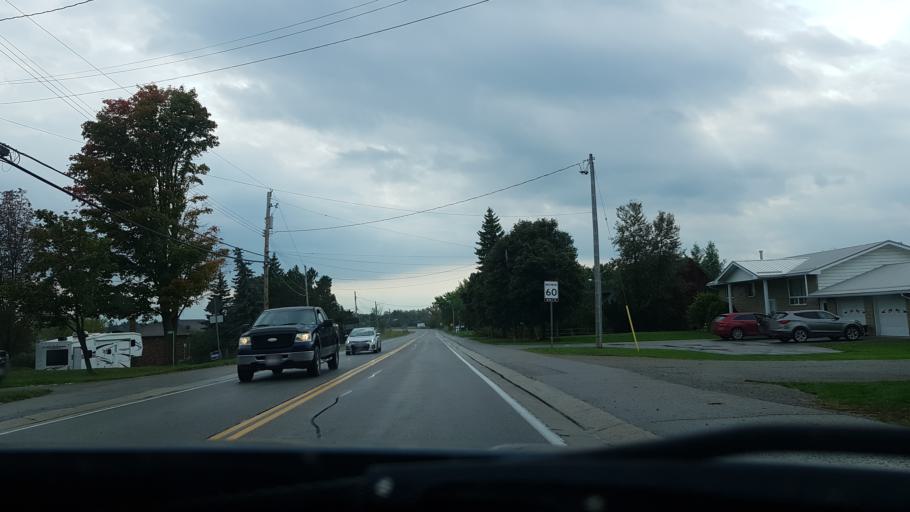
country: CA
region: Ontario
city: Omemee
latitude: 44.4382
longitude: -78.7753
